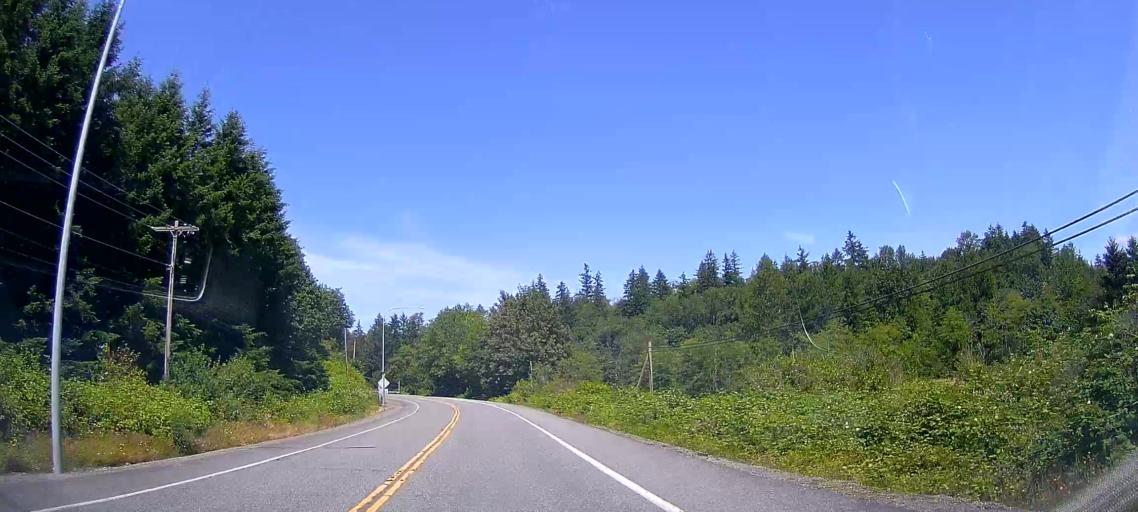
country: US
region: Washington
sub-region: Skagit County
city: Burlington
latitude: 48.5595
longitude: -122.3318
